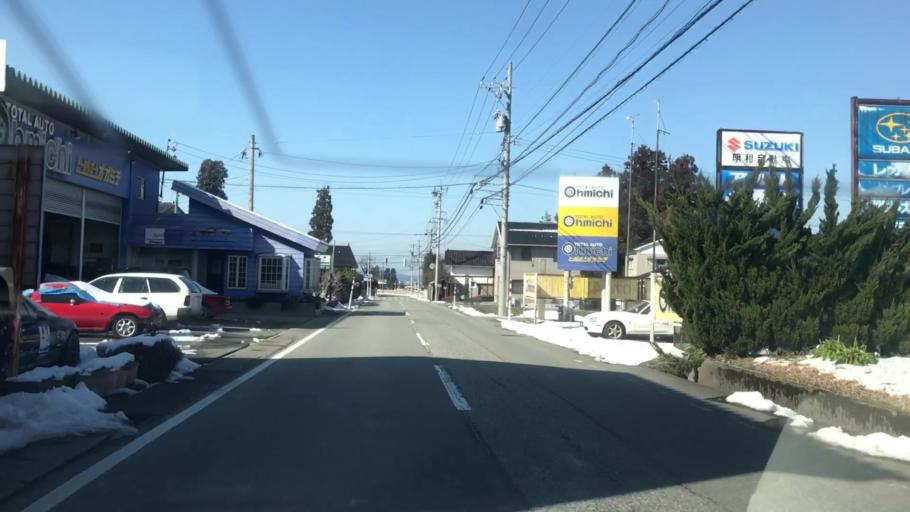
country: JP
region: Toyama
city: Toyama-shi
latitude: 36.6267
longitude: 137.2760
